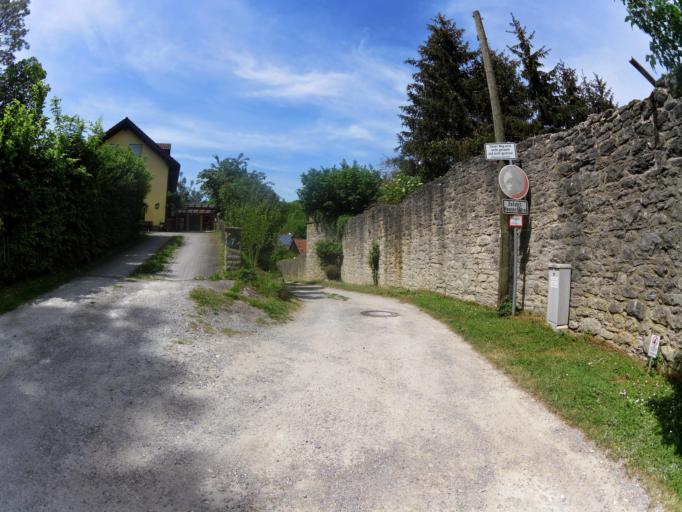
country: DE
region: Bavaria
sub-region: Regierungsbezirk Unterfranken
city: Sommerhausen
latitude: 49.6798
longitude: 10.0277
